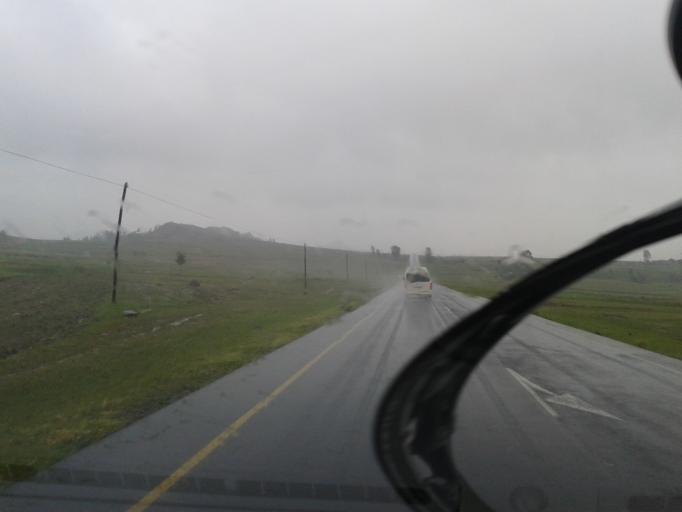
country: LS
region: Mafeteng
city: Mafeteng
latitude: -29.6720
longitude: 27.4501
